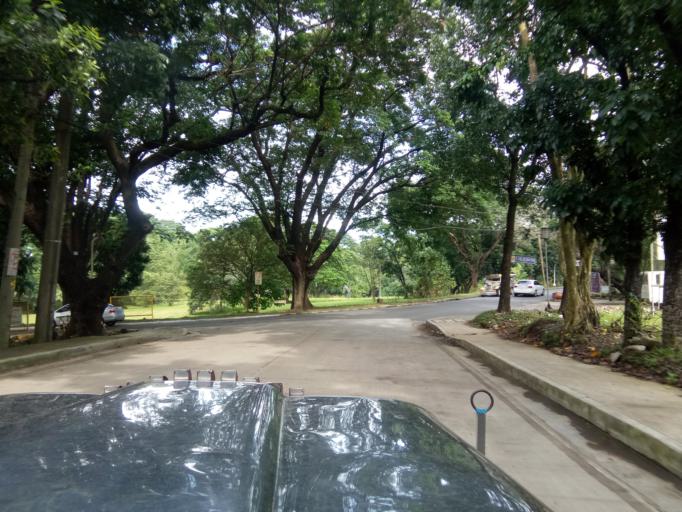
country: PH
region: Metro Manila
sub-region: Quezon City
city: Quezon City
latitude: 14.6530
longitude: 121.0646
